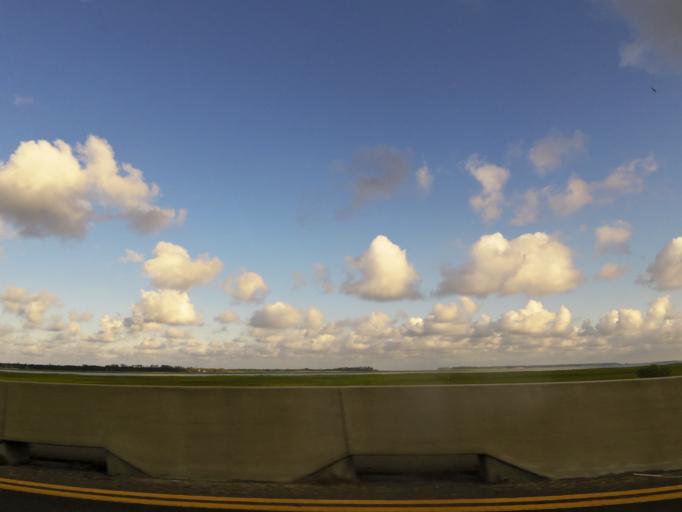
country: US
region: Georgia
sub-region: Glynn County
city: Saint Simon Mills
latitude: 31.1706
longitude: -81.4329
